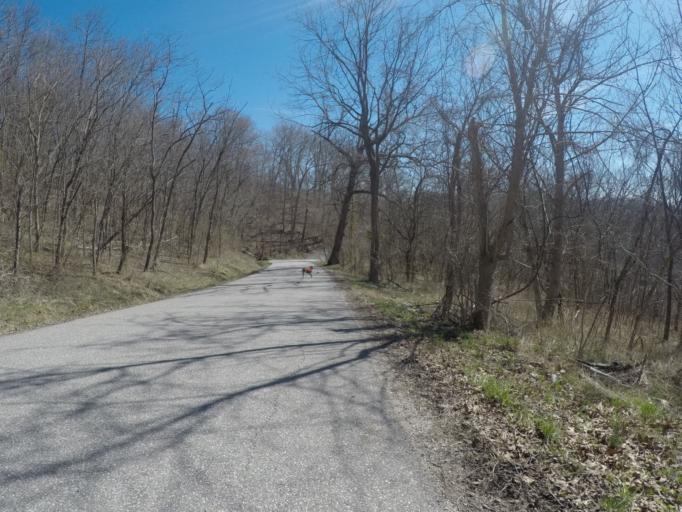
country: US
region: Ohio
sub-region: Lawrence County
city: South Point
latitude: 38.4808
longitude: -82.5664
